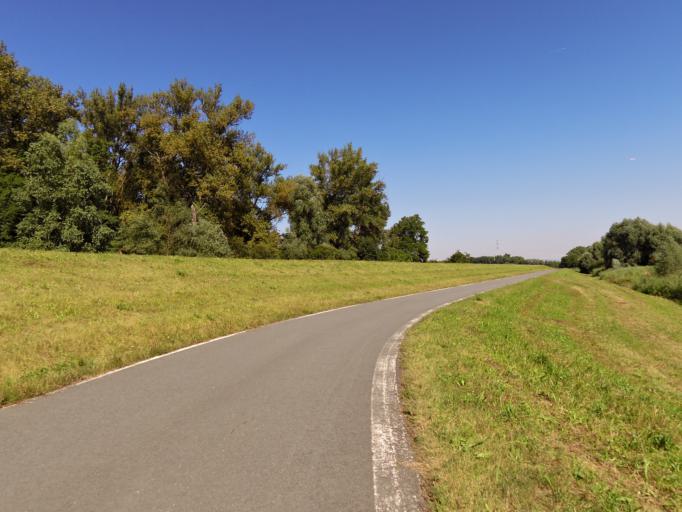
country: DE
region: Hesse
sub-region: Regierungsbezirk Darmstadt
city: Ginsheim-Gustavsburg
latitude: 49.9499
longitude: 8.3587
